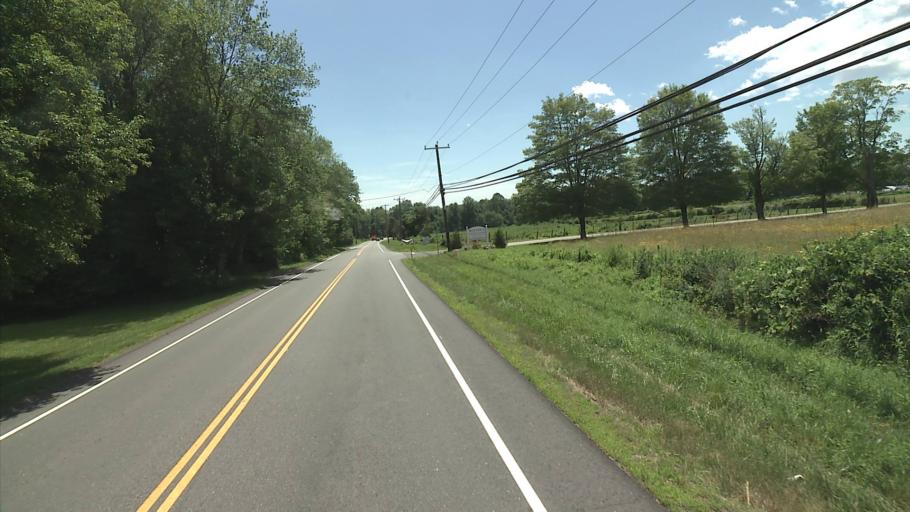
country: US
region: Connecticut
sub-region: Middlesex County
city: East Haddam
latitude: 41.4720
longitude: -72.4443
